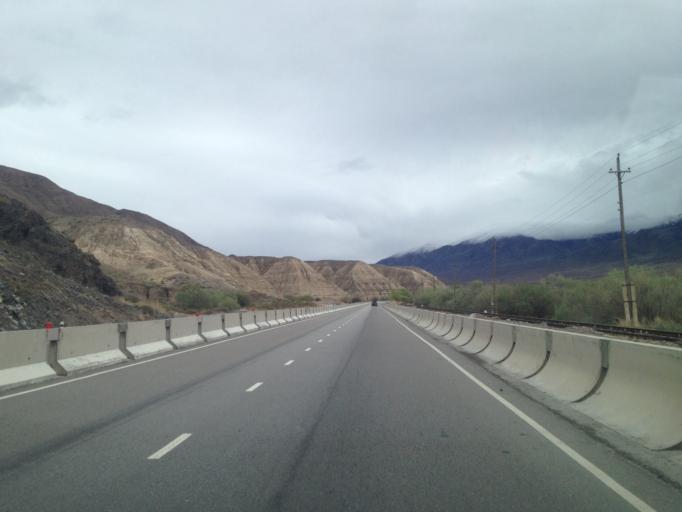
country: KG
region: Naryn
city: Kochkor
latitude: 42.4945
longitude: 75.8490
